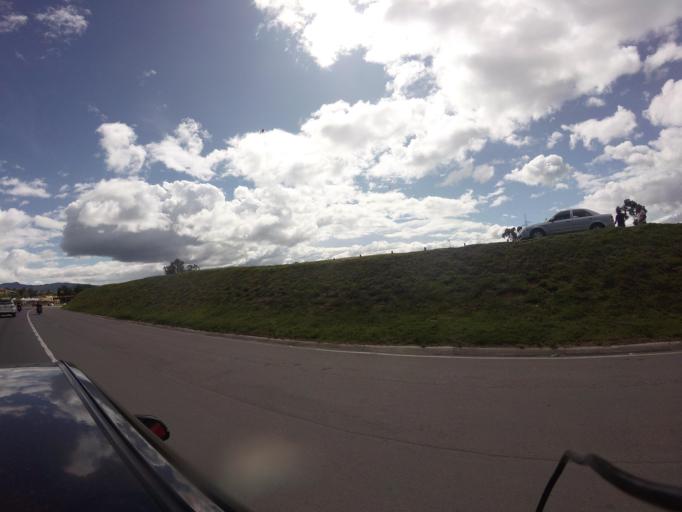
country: CO
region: Cundinamarca
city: Tocancipa
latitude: 4.9600
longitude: -73.9123
